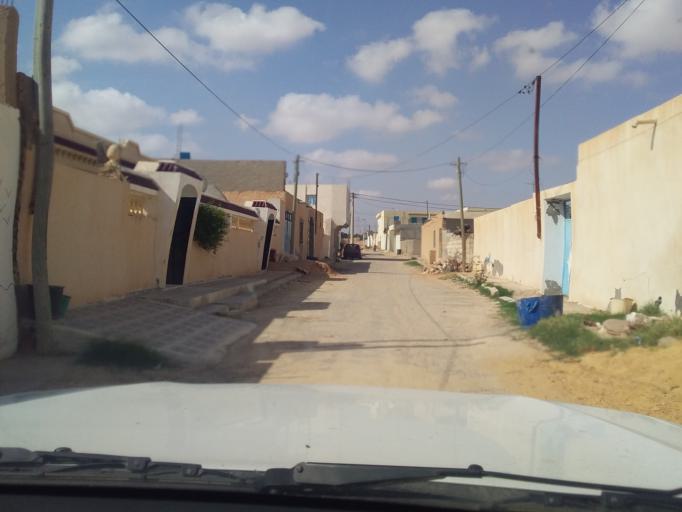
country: TN
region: Madanin
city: Medenine
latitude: 33.5827
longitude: 10.3231
